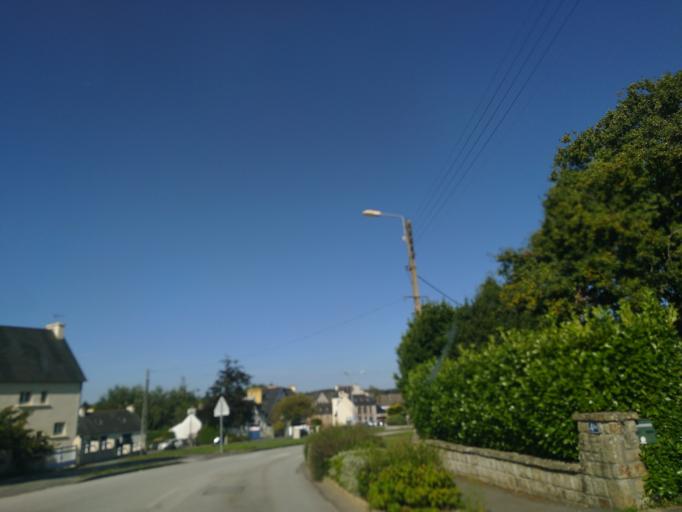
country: FR
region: Brittany
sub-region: Departement du Finistere
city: Le Faou
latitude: 48.2923
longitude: -4.1807
